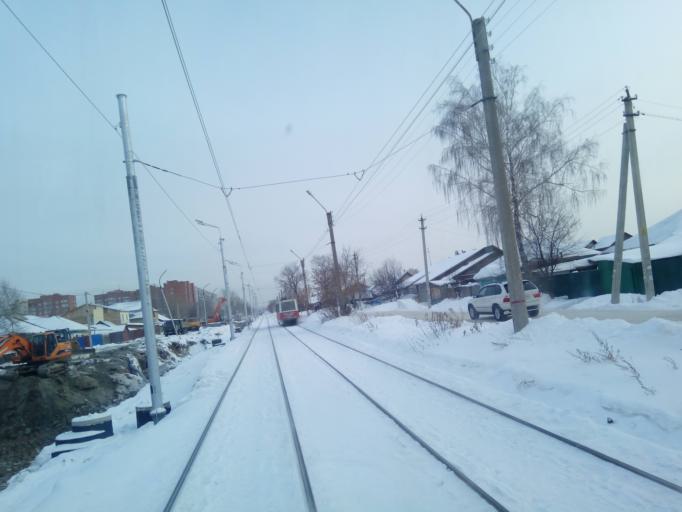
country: RU
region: Novosibirsk
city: Tolmachevo
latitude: 54.9795
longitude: 82.8199
